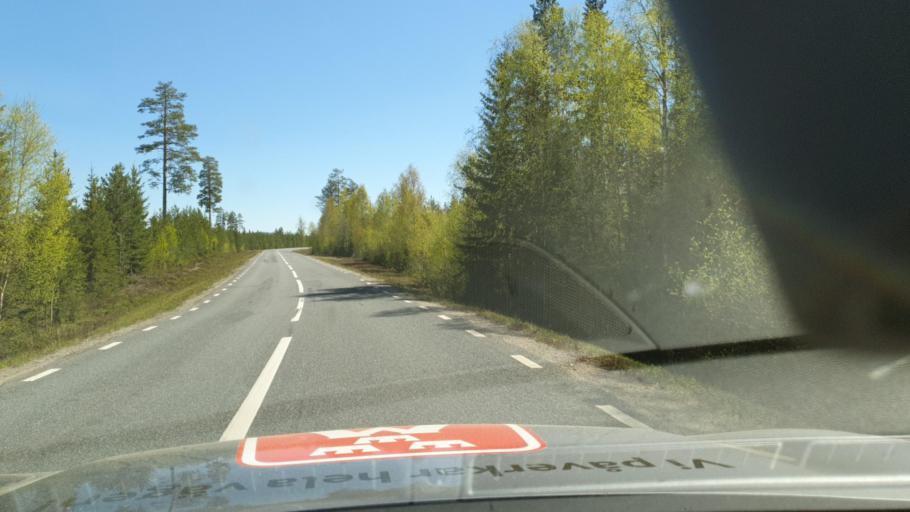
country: SE
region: Vaesternorrland
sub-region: OErnskoeldsviks Kommun
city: Bredbyn
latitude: 63.8451
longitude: 18.4730
